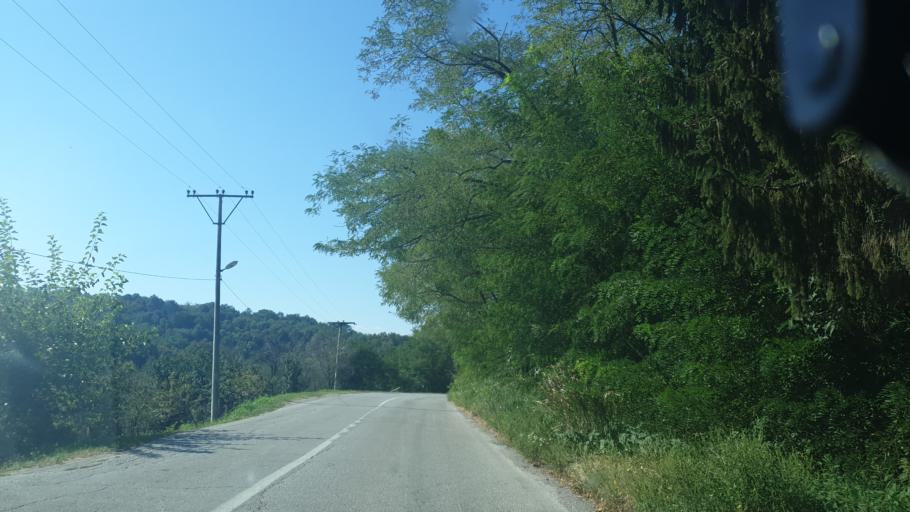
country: RS
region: Central Serbia
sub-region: Kolubarski Okrug
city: Lajkovac
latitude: 44.3237
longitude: 20.1936
